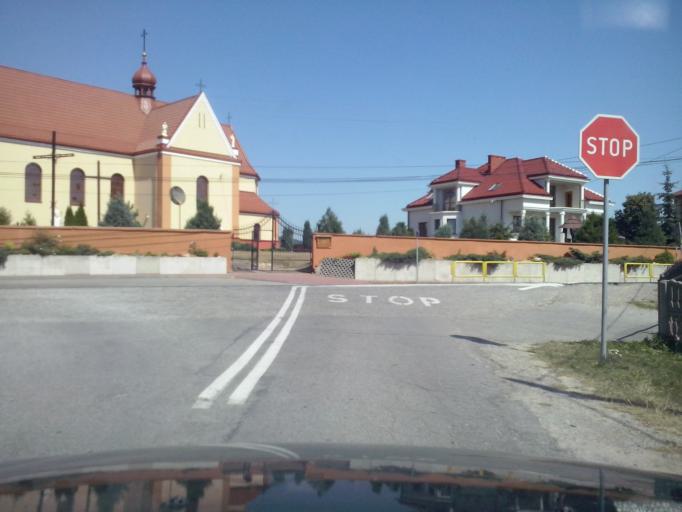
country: PL
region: Swietokrzyskie
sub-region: Powiat kielecki
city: Bieliny
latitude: 50.8086
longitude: 20.9603
